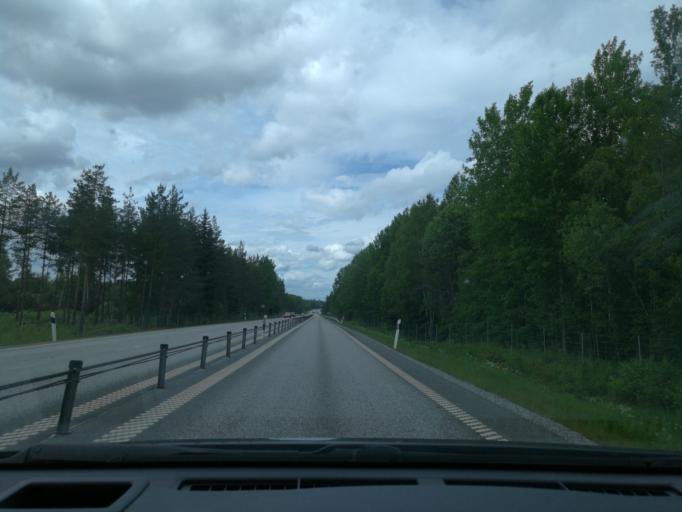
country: SE
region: Vaestmanland
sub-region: Surahammars Kommun
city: Surahammar
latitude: 59.7158
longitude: 16.2417
